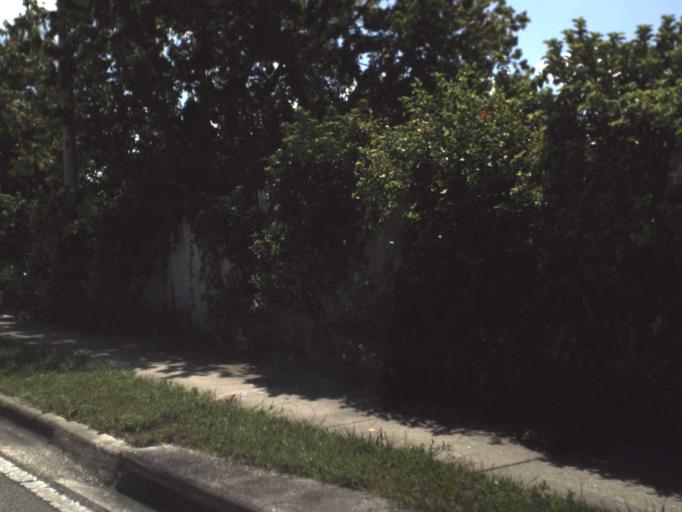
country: US
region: Florida
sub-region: Pinellas County
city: Oldsmar
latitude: 28.0377
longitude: -82.6771
